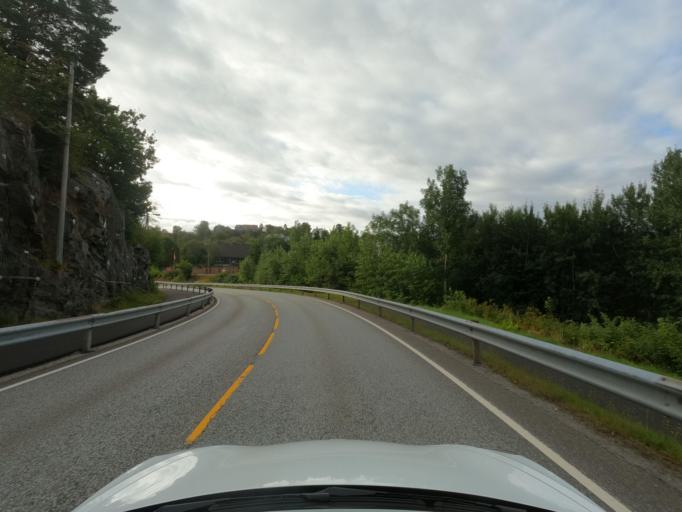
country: NO
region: Hordaland
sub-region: Bergen
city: Sandsli
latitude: 60.3108
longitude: 5.2924
